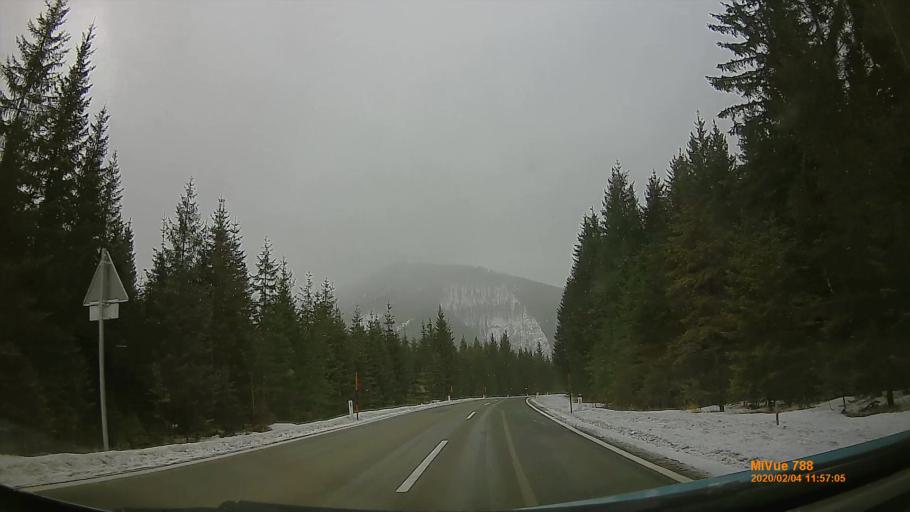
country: AT
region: Styria
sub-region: Politischer Bezirk Bruck-Muerzzuschlag
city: Muerzsteg
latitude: 47.7668
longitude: 15.5121
